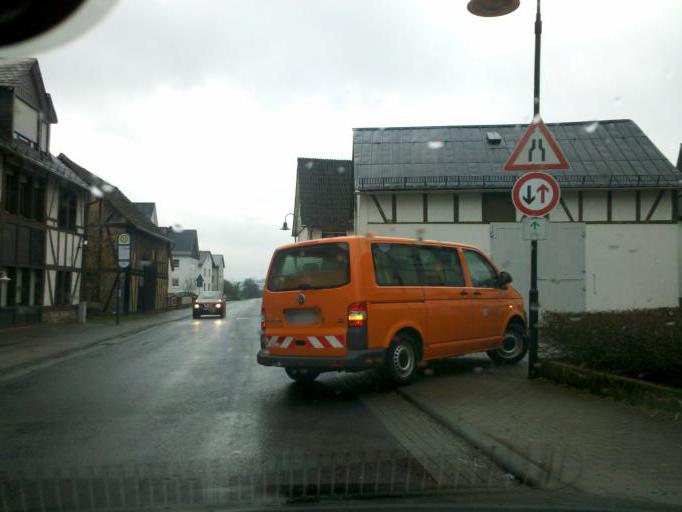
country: DE
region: Hesse
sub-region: Regierungsbezirk Giessen
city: Haiger
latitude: 50.7896
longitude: 8.2271
